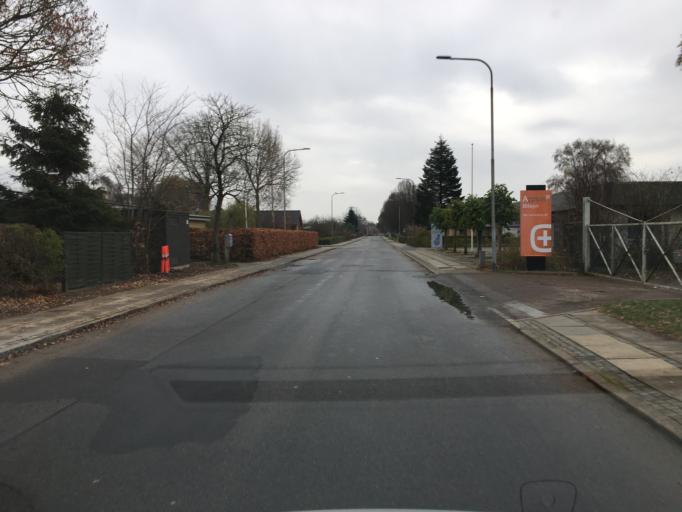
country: DK
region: South Denmark
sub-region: Tonder Kommune
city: Tonder
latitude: 54.9450
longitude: 8.8611
